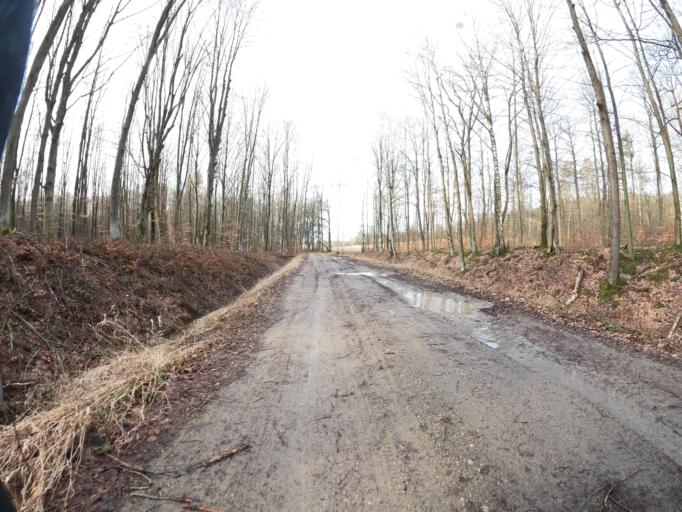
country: PL
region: West Pomeranian Voivodeship
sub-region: Powiat koszalinski
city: Polanow
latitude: 54.1725
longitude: 16.7491
